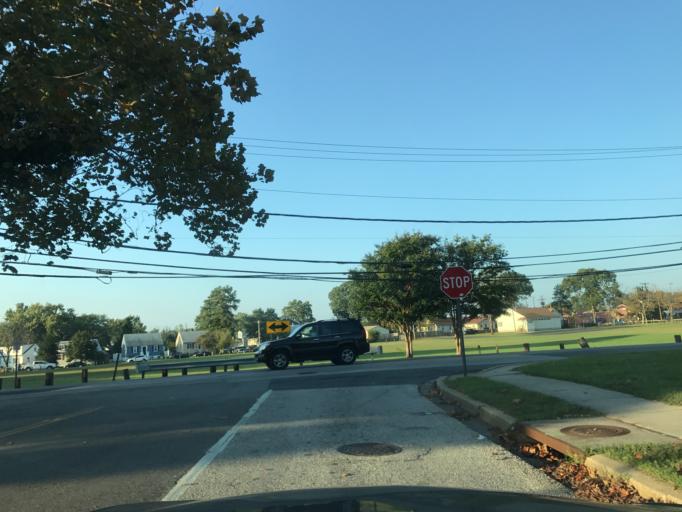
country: US
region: Maryland
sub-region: Anne Arundel County
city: Glen Burnie
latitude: 39.1570
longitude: -76.6225
